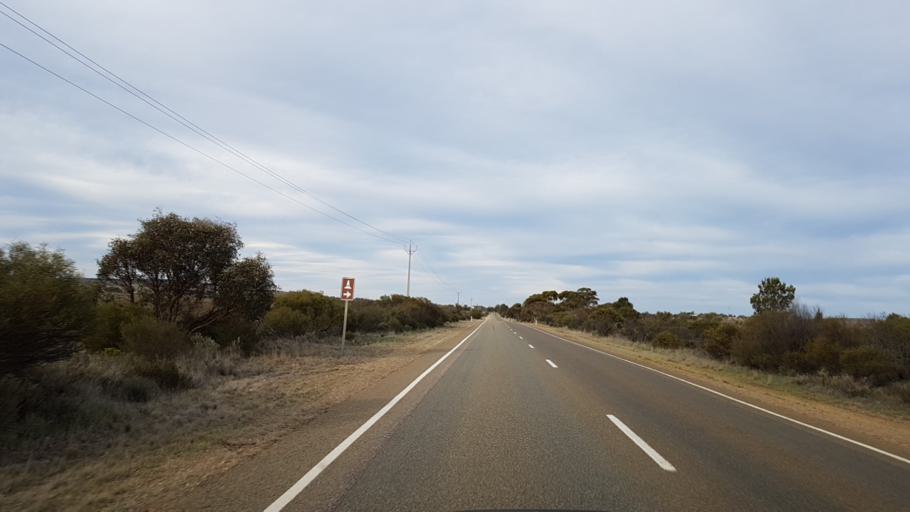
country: AU
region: South Australia
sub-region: Peterborough
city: Peterborough
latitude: -32.9851
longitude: 138.8044
